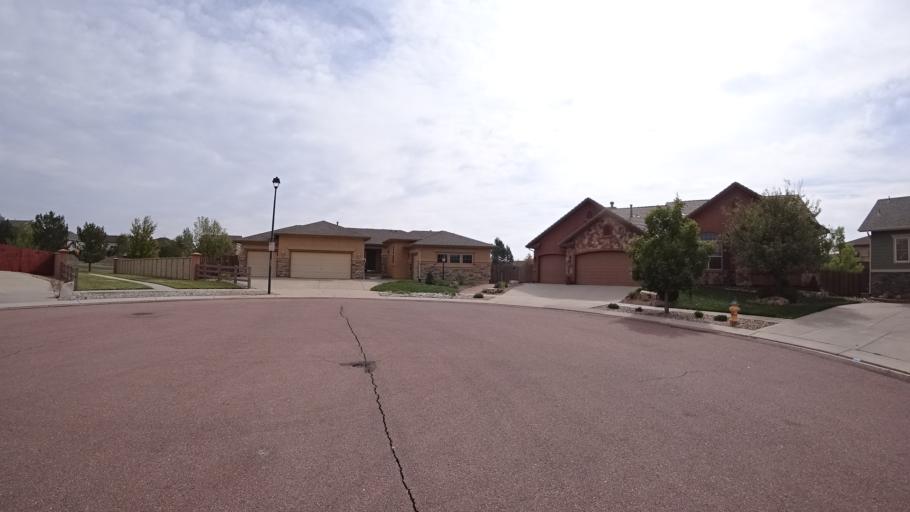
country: US
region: Colorado
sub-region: El Paso County
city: Cimarron Hills
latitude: 38.9244
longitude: -104.6933
